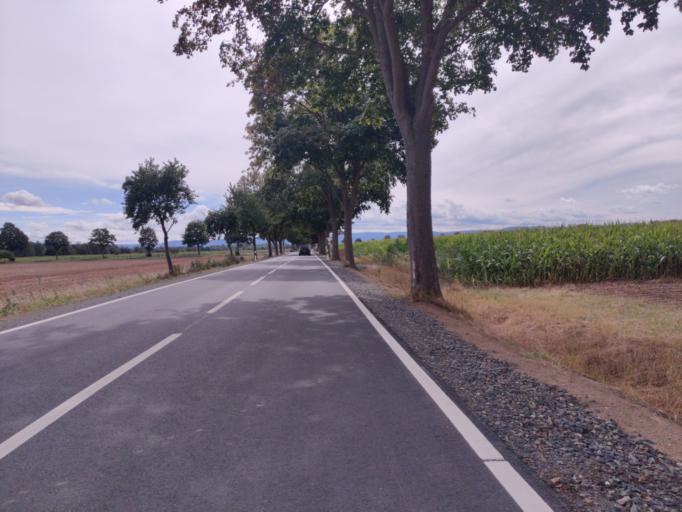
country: DE
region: Lower Saxony
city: Liebenburg
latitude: 52.0078
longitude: 10.3684
